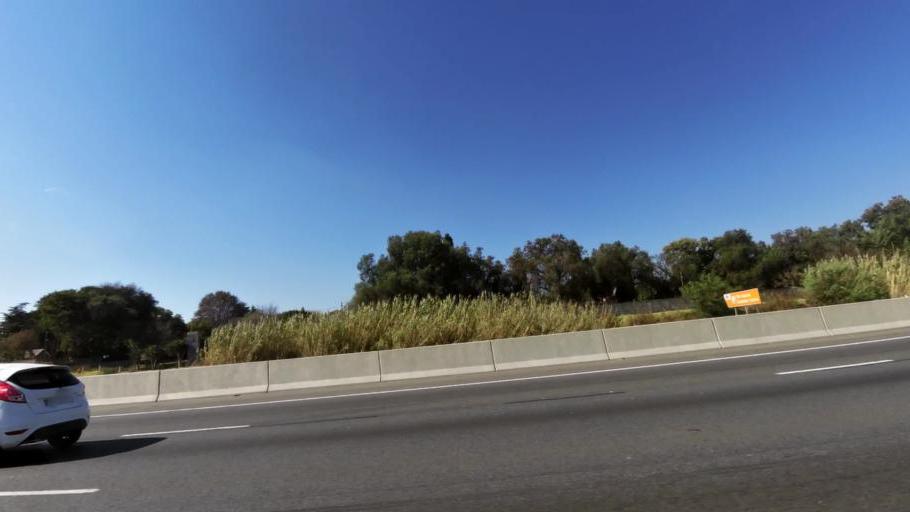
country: ZA
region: Gauteng
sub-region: City of Johannesburg Metropolitan Municipality
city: Roodepoort
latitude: -26.1413
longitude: 27.9324
